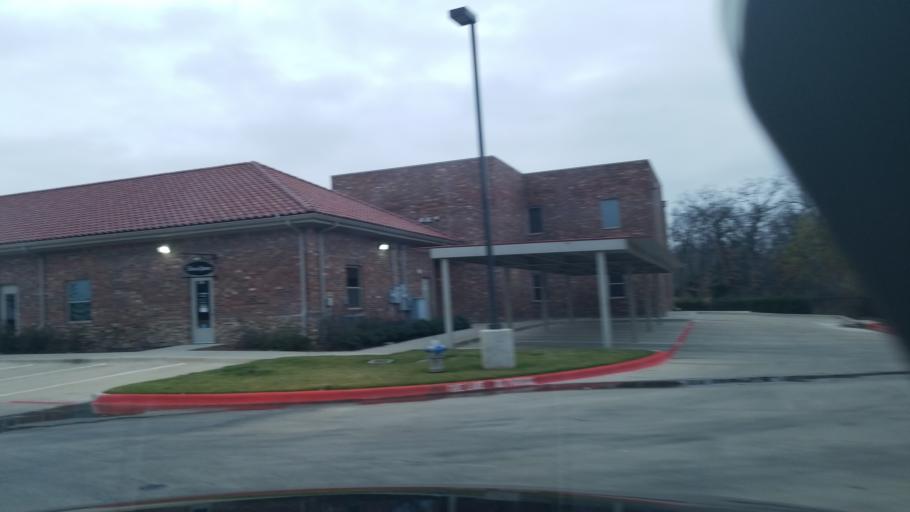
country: US
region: Texas
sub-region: Denton County
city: Hickory Creek
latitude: 33.1310
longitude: -97.0638
